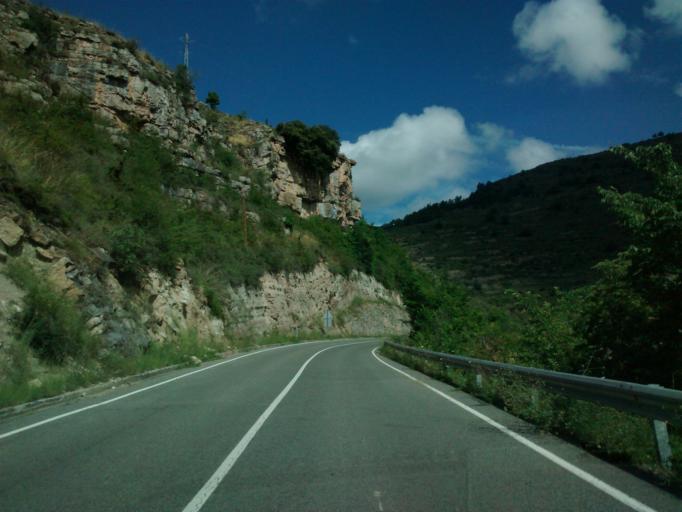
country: ES
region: La Rioja
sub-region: Provincia de La Rioja
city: Soto en Cameros
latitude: 42.2902
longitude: -2.4252
